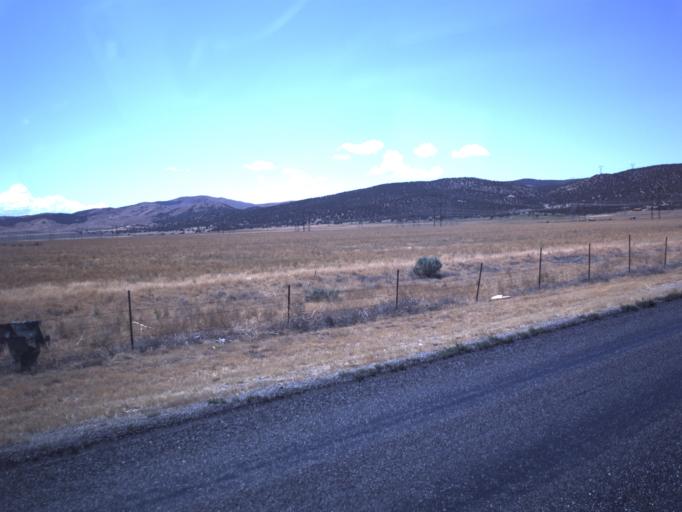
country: US
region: Utah
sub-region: Juab County
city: Nephi
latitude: 39.7088
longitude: -111.9023
